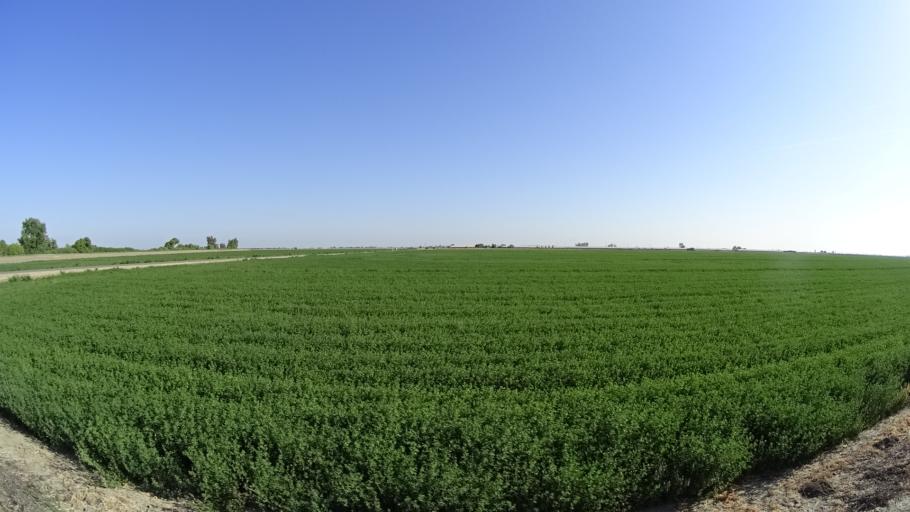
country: US
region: California
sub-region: Fresno County
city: Riverdale
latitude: 36.4014
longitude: -119.9225
